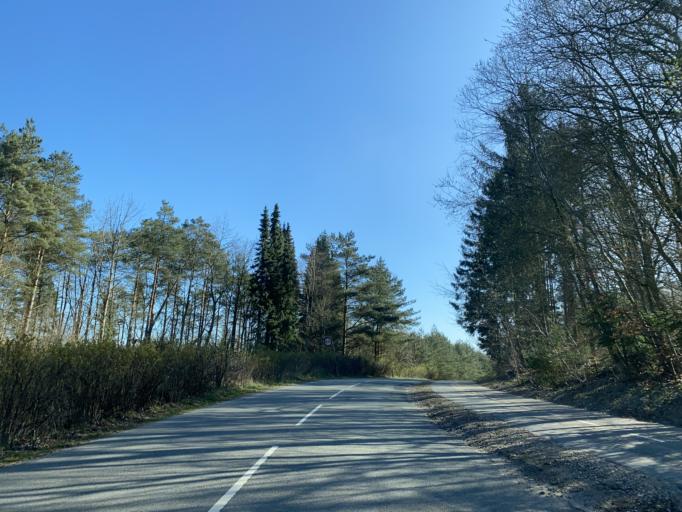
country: DK
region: Central Jutland
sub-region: Favrskov Kommune
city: Ulstrup
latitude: 56.3846
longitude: 9.7586
